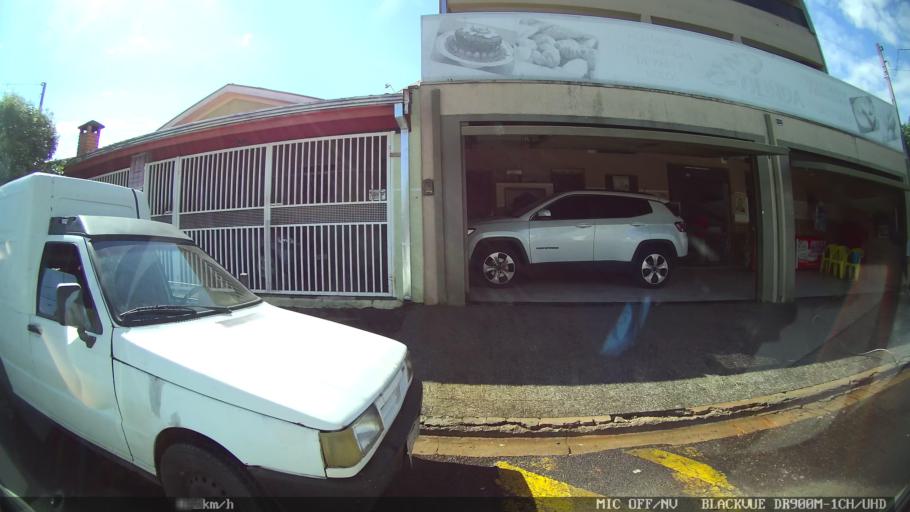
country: BR
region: Sao Paulo
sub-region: Santa Barbara D'Oeste
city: Santa Barbara d'Oeste
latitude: -22.7382
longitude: -47.3877
